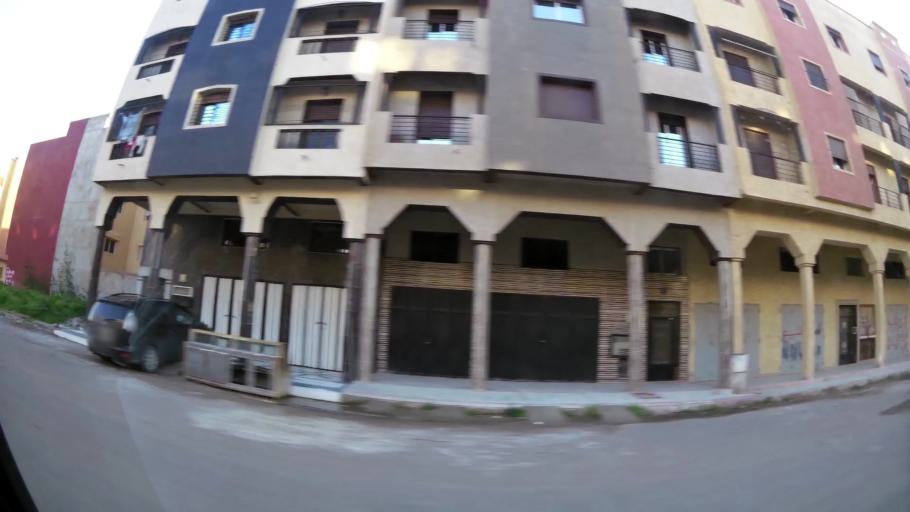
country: MA
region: Chaouia-Ouardigha
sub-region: Settat Province
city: Settat
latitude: 32.9884
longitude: -7.5986
